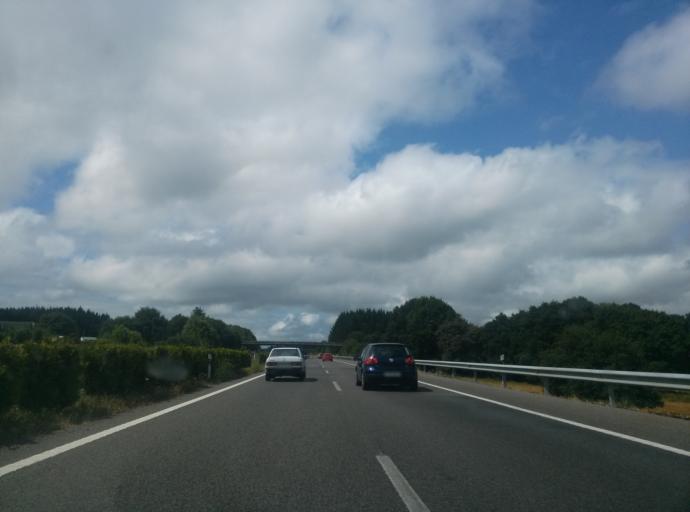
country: ES
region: Galicia
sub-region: Provincia de Lugo
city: Outeiro de Rei
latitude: 43.0795
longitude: -7.5790
